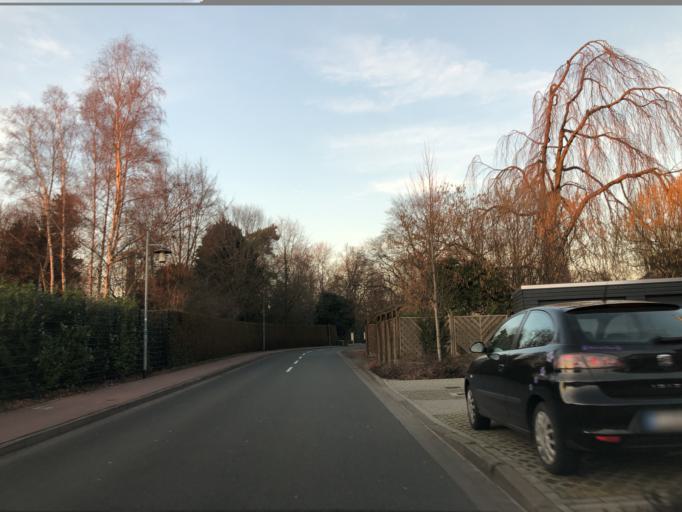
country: DE
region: Lower Saxony
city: Papenburg
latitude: 53.0868
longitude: 7.3906
